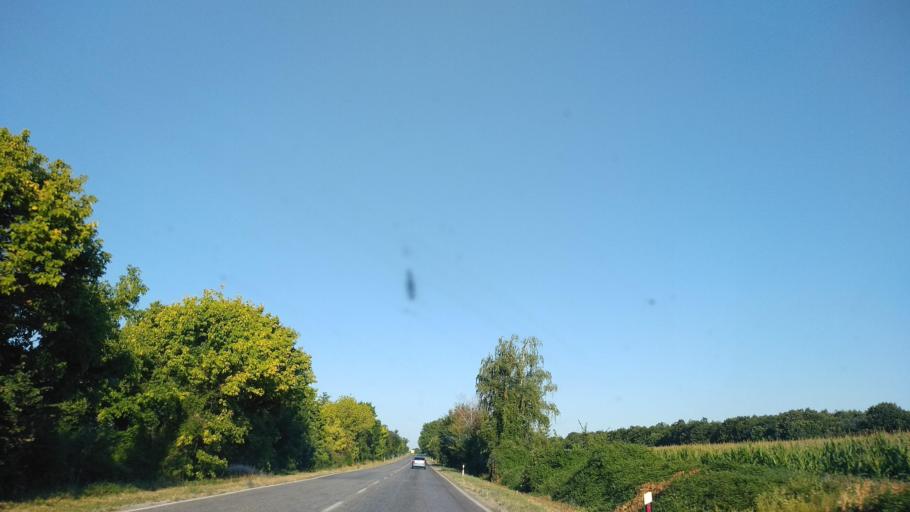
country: BG
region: Gabrovo
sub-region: Obshtina Dryanovo
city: Dryanovo
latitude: 43.0874
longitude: 25.4483
